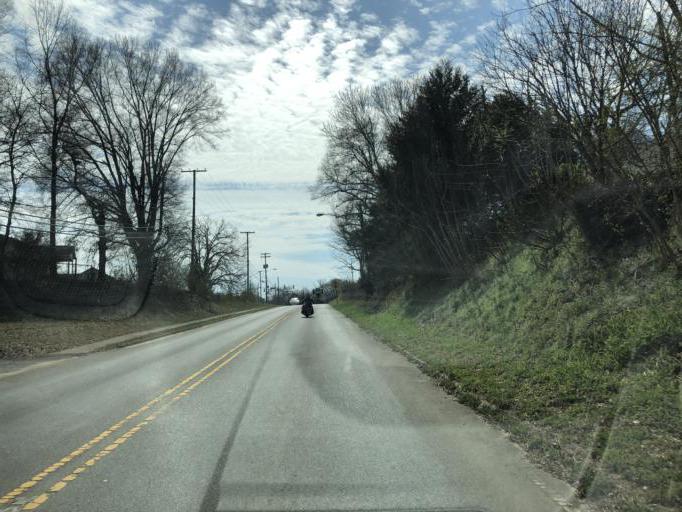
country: US
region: North Carolina
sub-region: Gaston County
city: Dallas
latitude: 35.3177
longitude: -81.1672
